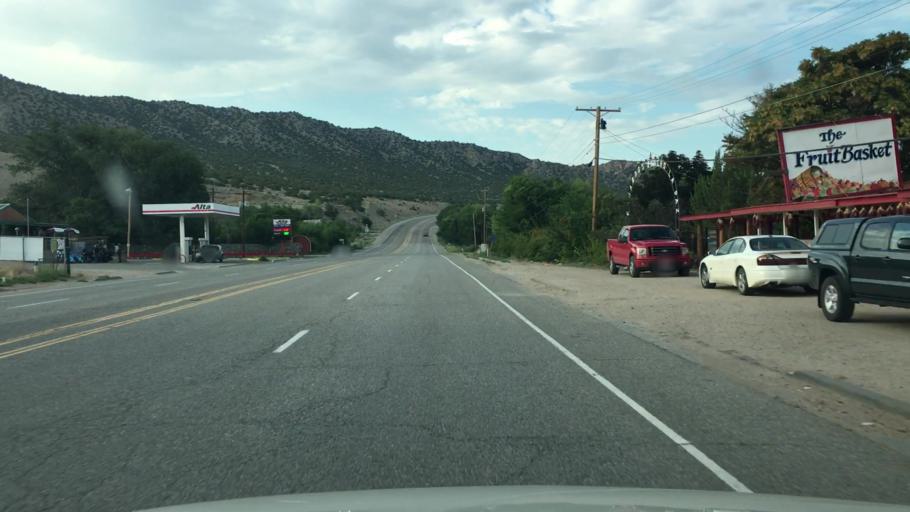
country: US
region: New Mexico
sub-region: Rio Arriba County
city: Ohkay Owingeh
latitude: 36.1656
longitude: -105.9680
